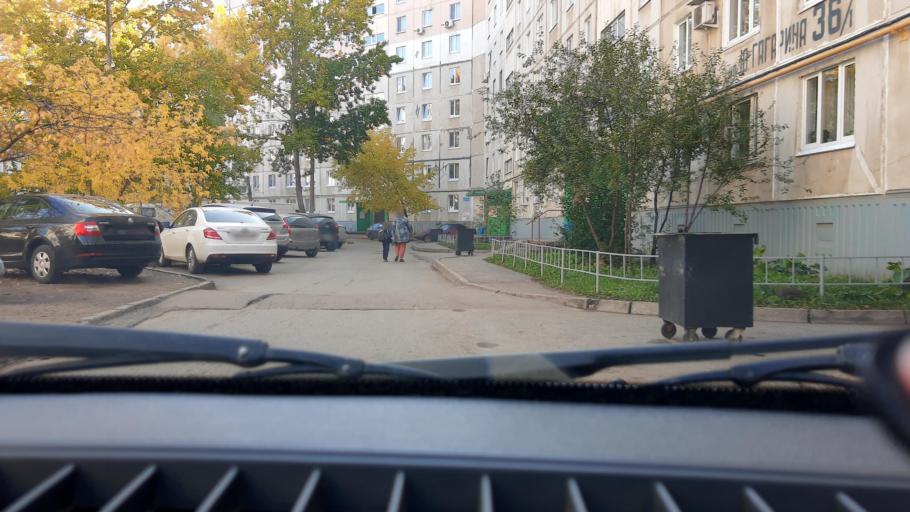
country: RU
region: Bashkortostan
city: Ufa
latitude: 54.7652
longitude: 56.0692
